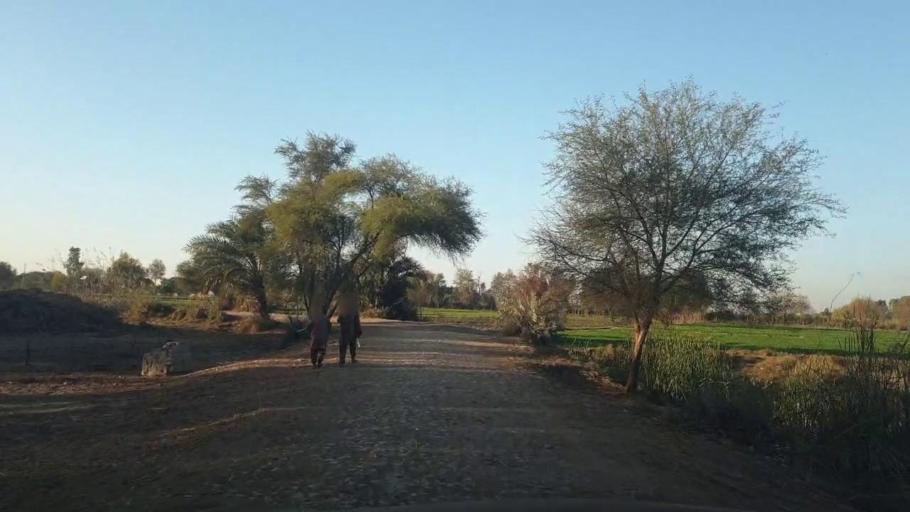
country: PK
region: Sindh
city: Mirpur Mathelo
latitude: 28.0054
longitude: 69.4649
